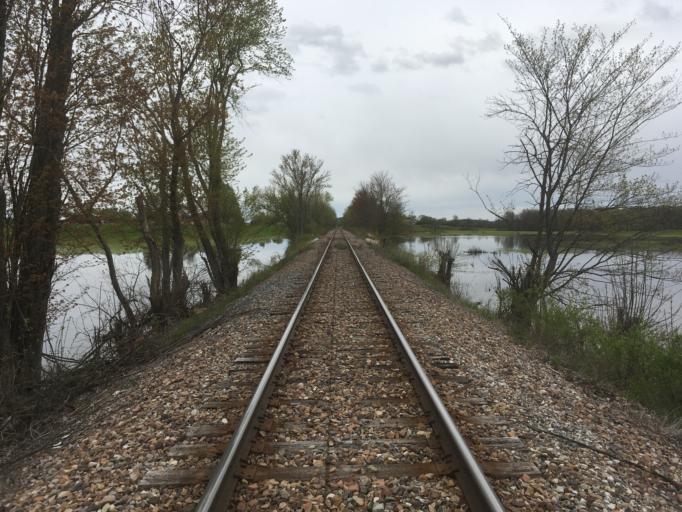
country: US
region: Vermont
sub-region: Addison County
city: Middlebury (village)
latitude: 43.9611
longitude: -73.1624
